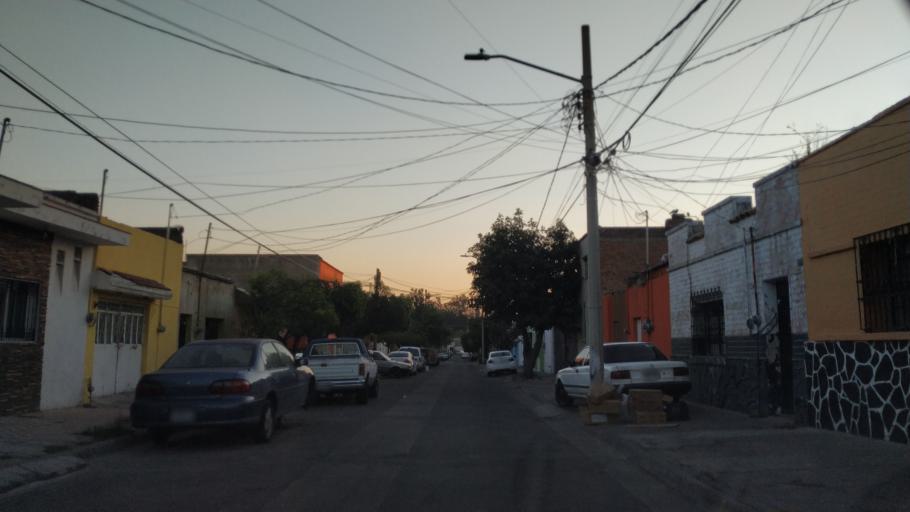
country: MX
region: Jalisco
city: Tlaquepaque
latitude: 20.6528
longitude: -103.3325
